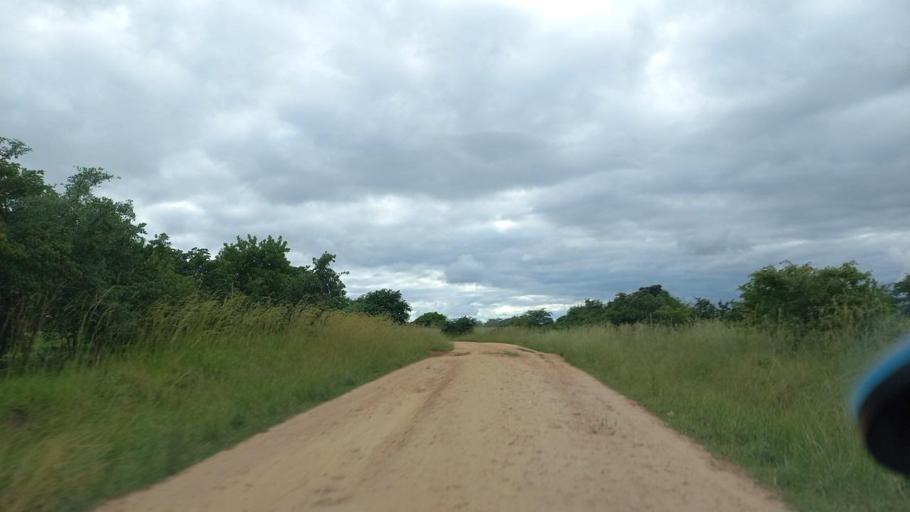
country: ZM
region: Lusaka
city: Chongwe
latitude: -15.4495
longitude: 28.8364
